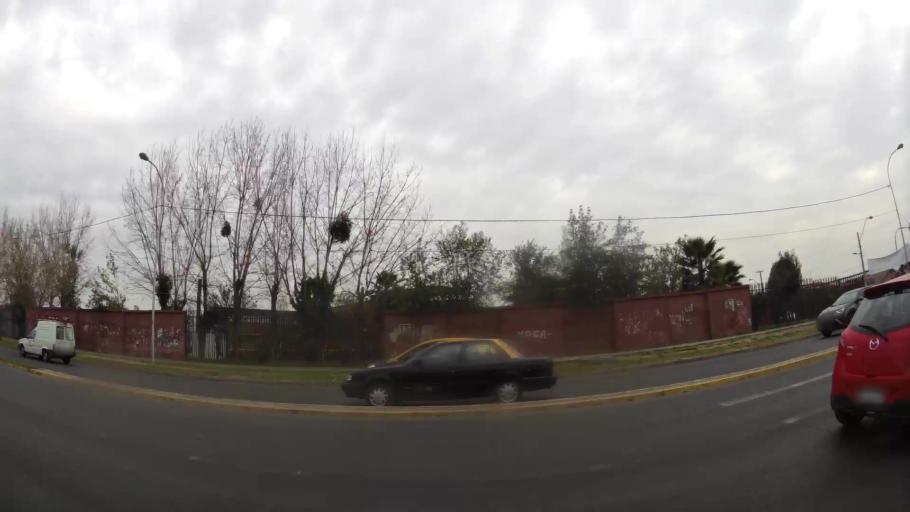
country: CL
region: Santiago Metropolitan
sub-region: Provincia de Santiago
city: Villa Presidente Frei, Nunoa, Santiago, Chile
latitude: -33.5024
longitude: -70.6031
